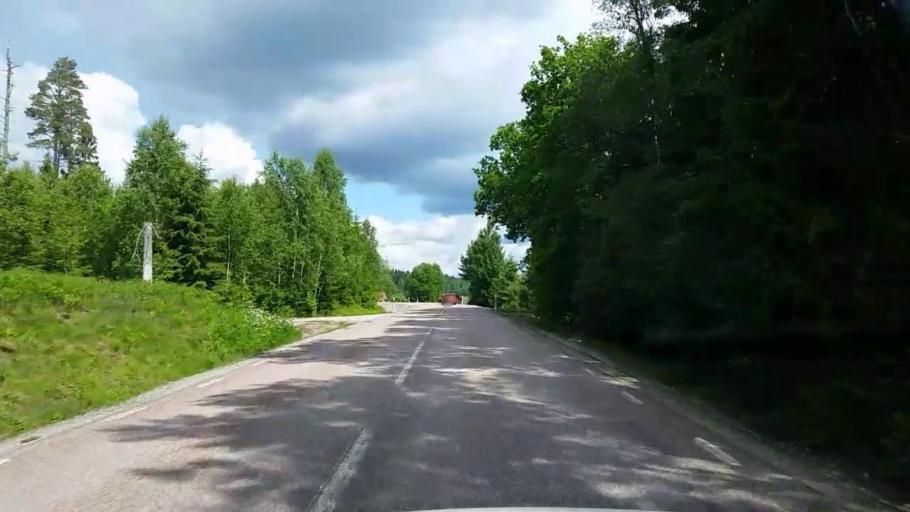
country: SE
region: Vaestmanland
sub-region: Skinnskattebergs Kommun
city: Skinnskatteberg
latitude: 59.7953
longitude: 15.8479
